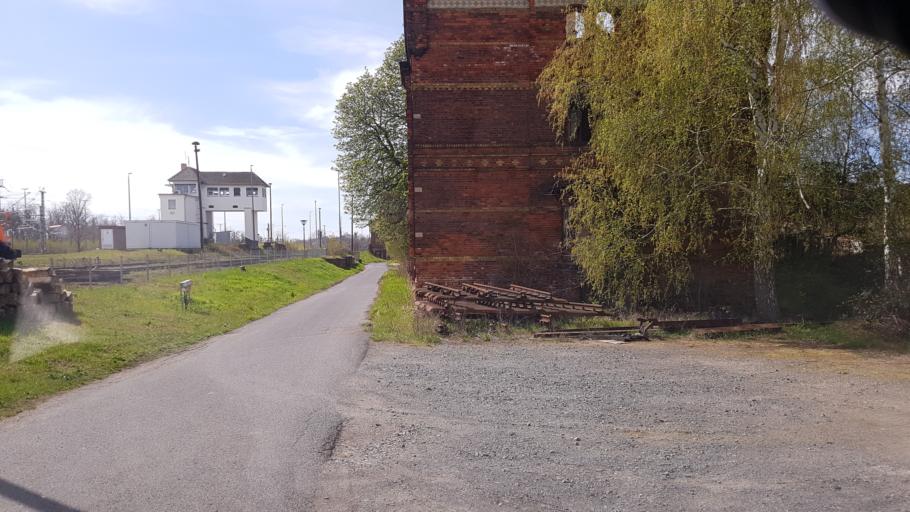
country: DE
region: Brandenburg
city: Falkenberg
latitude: 51.5835
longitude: 13.2660
